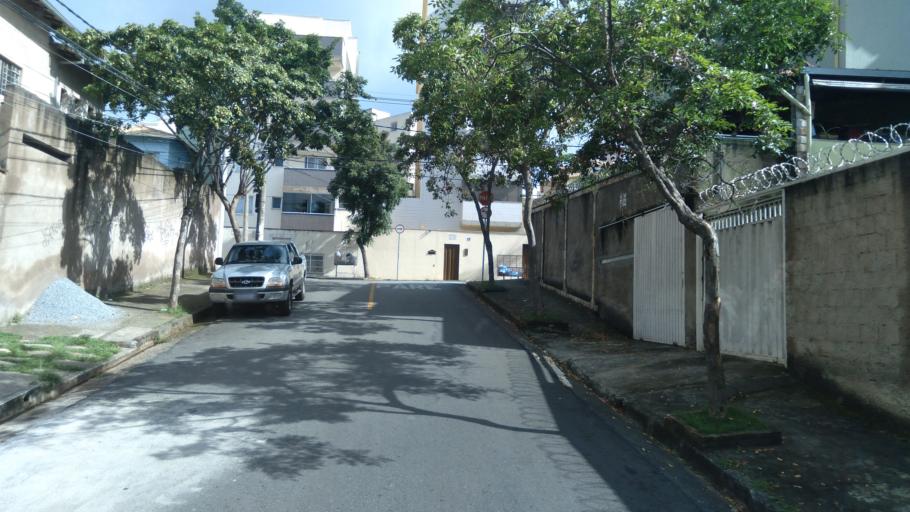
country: BR
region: Minas Gerais
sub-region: Belo Horizonte
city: Belo Horizonte
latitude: -19.8877
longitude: -43.8917
